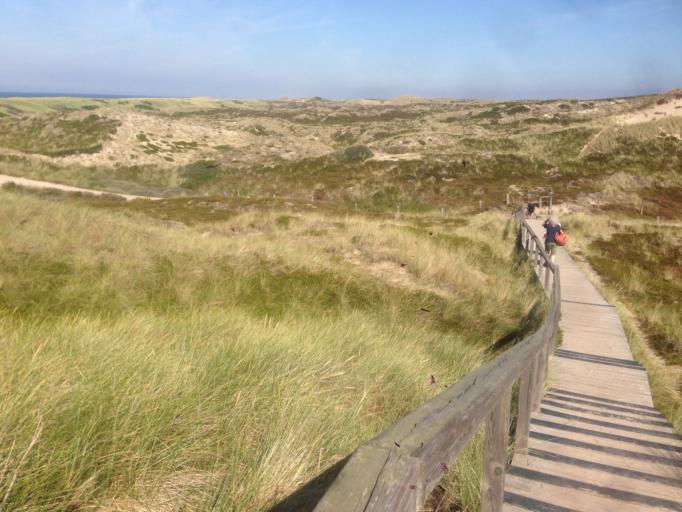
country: DE
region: Schleswig-Holstein
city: Tinnum
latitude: 54.9657
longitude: 8.3379
